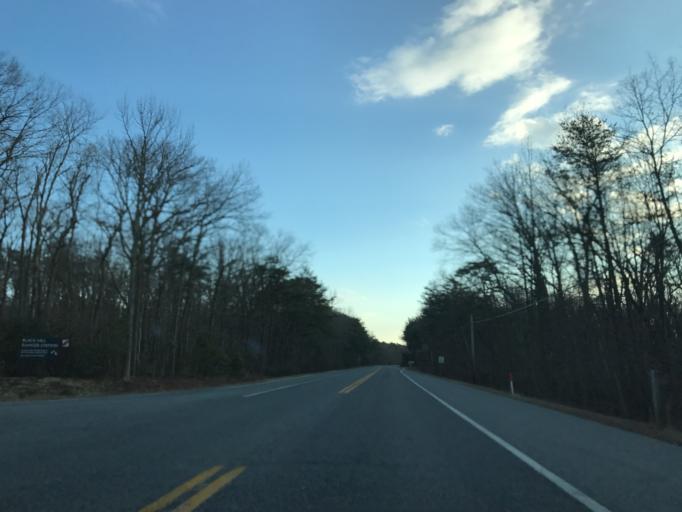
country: US
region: Maryland
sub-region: Cecil County
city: Charlestown
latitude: 39.5490
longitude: -75.9481
